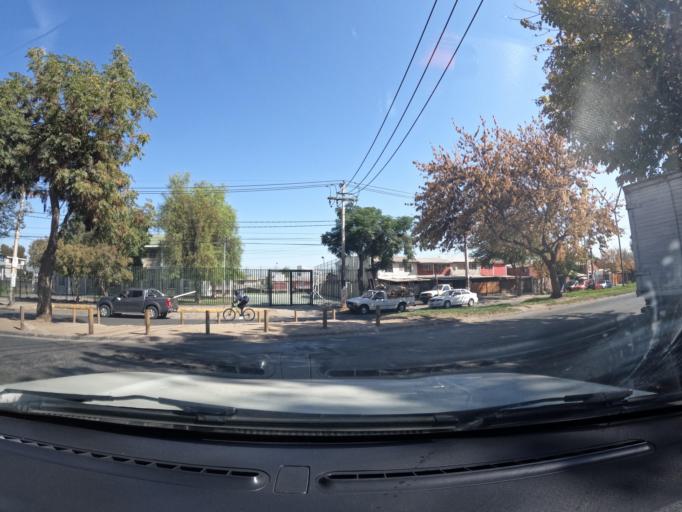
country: CL
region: Santiago Metropolitan
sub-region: Provincia de Santiago
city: Villa Presidente Frei, Nunoa, Santiago, Chile
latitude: -33.4808
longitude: -70.5665
